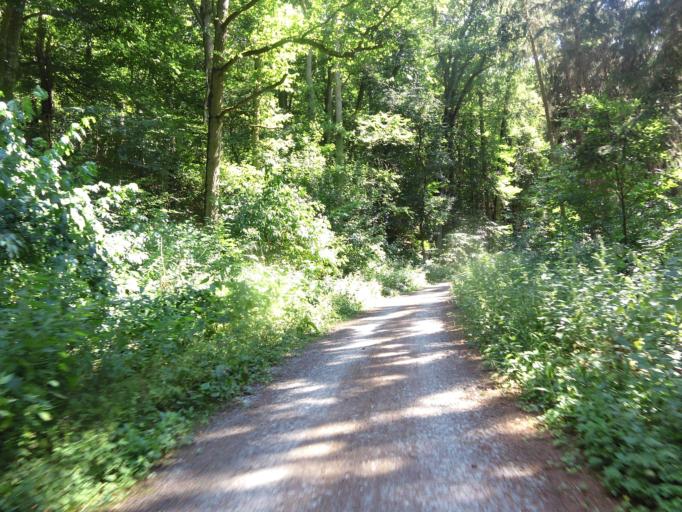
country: DE
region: Bavaria
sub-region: Regierungsbezirk Unterfranken
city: Gadheim
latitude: 49.8436
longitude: 9.9209
